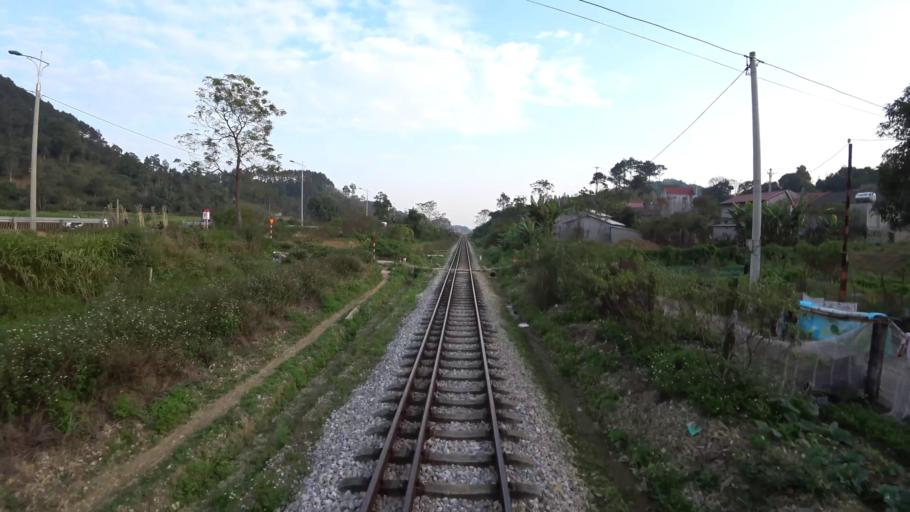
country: VN
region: Lang Son
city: Thi Tran Cao Loc
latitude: 21.9054
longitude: 106.7350
